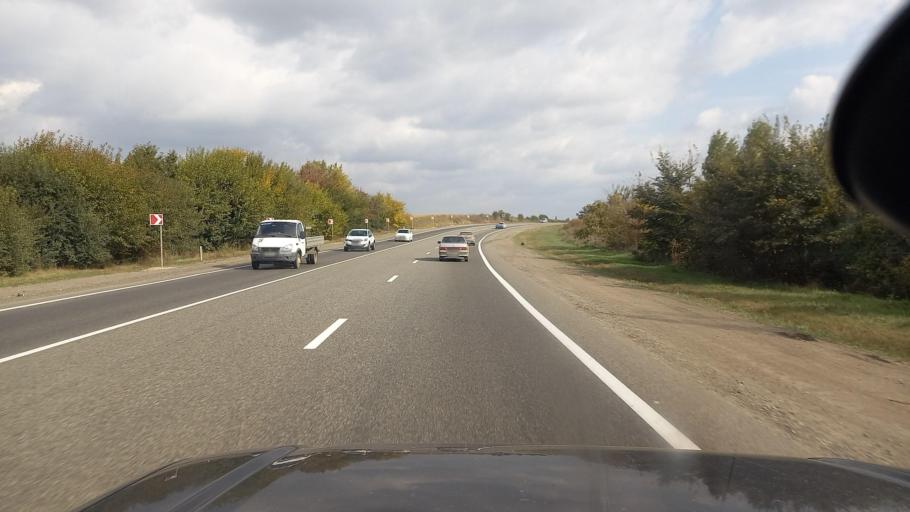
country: RU
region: Krasnodarskiy
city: Chernomorskiy
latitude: 44.8574
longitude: 38.4628
